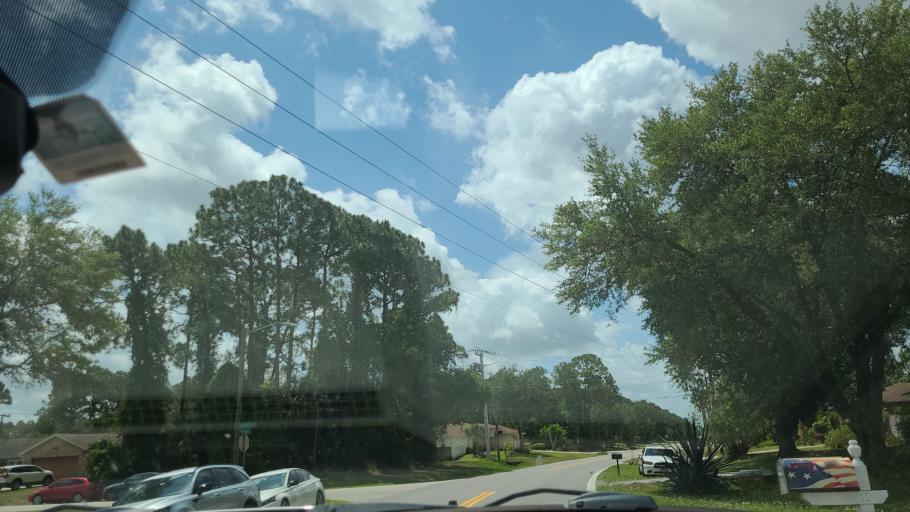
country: US
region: Florida
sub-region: Brevard County
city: June Park
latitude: 28.0073
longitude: -80.7167
